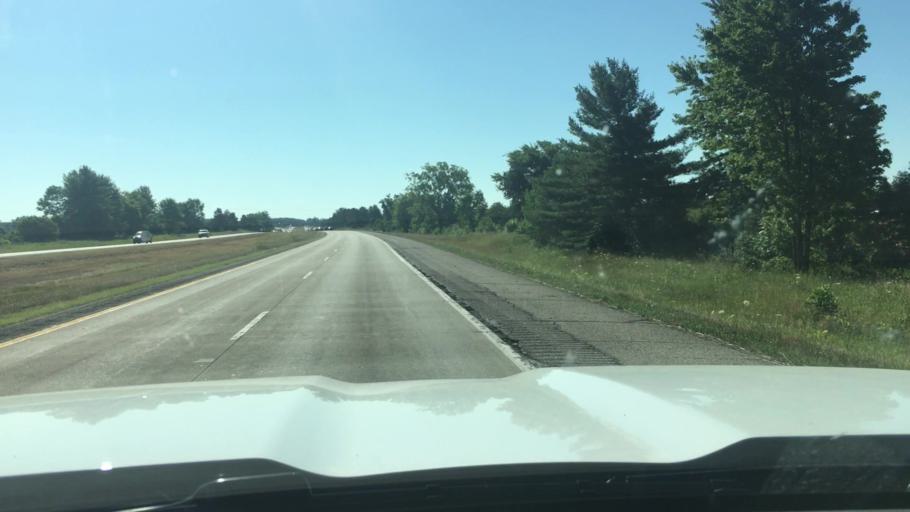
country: US
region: Michigan
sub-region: Eaton County
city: Grand Ledge
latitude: 42.8049
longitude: -84.7600
